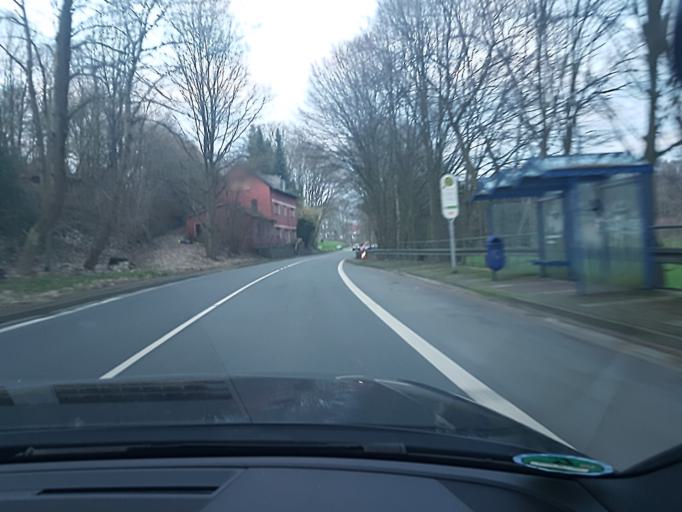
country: DE
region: North Rhine-Westphalia
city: Hattingen
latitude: 51.3820
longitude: 7.1940
